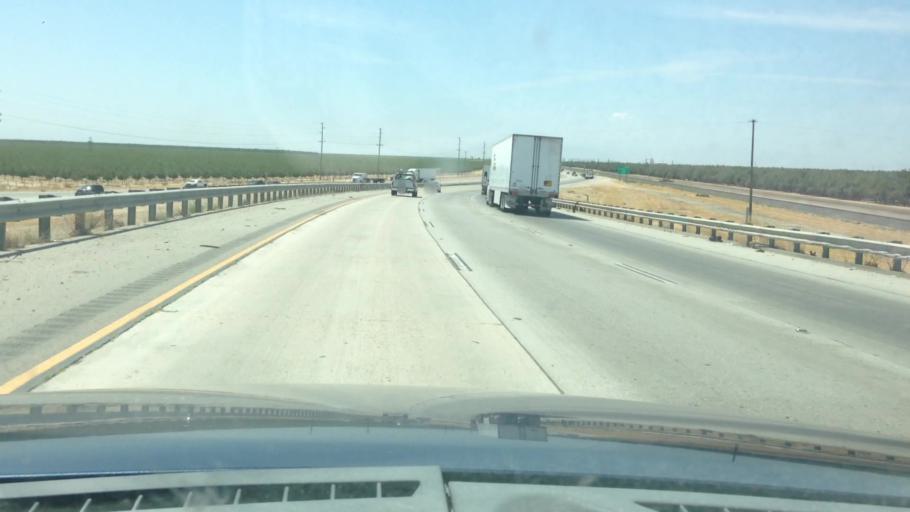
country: US
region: California
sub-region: Kern County
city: McFarland
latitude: 35.5891
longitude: -119.2051
